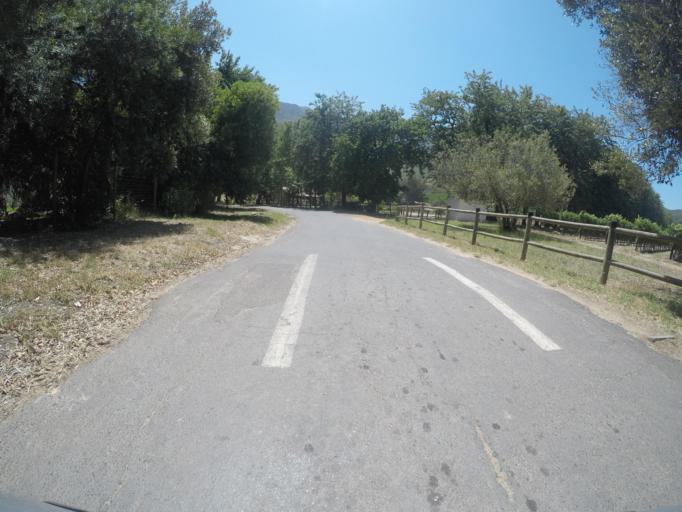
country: ZA
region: Western Cape
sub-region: Cape Winelands District Municipality
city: Stellenbosch
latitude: -33.9963
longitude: 18.8754
